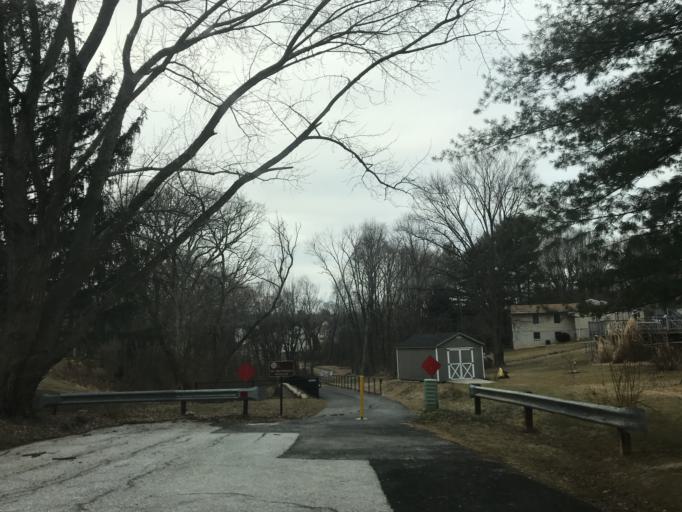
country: US
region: Maryland
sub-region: Carroll County
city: Eldersburg
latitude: 39.3966
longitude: -76.9405
